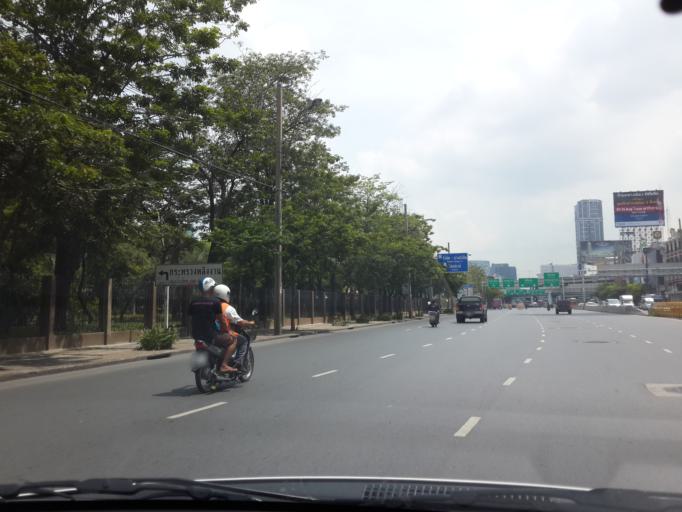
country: TH
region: Bangkok
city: Chatuchak
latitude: 13.8088
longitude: 100.5574
